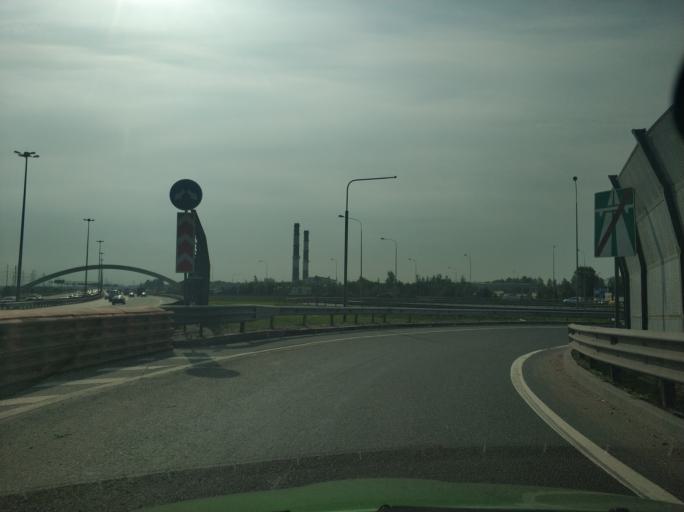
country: RU
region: Leningrad
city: Murino
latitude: 60.0352
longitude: 30.4404
